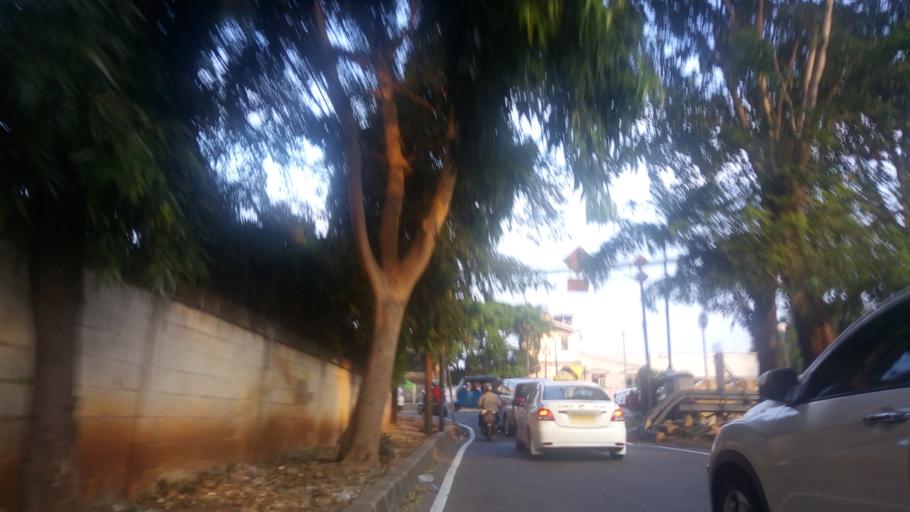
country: ID
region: Jakarta Raya
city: Jakarta
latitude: -6.2012
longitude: 106.8510
